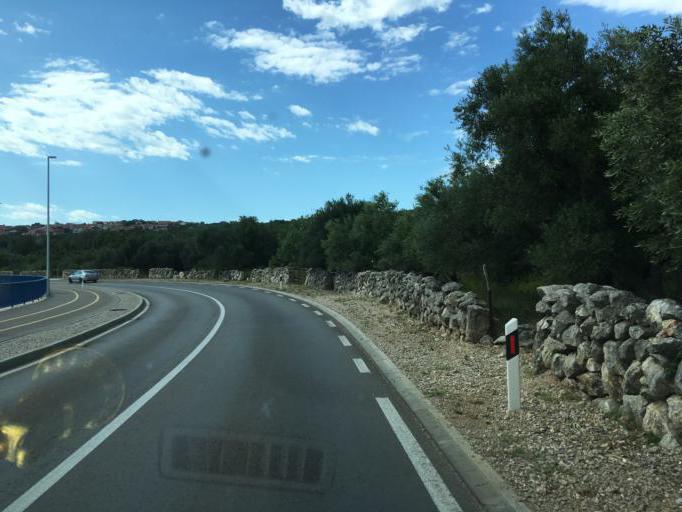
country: HR
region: Primorsko-Goranska
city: Punat
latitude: 45.0400
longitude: 14.6244
